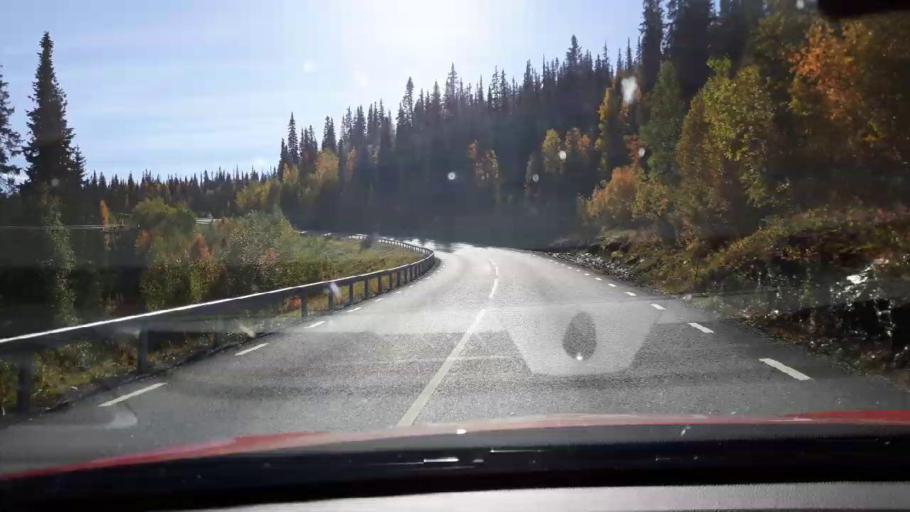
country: NO
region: Nord-Trondelag
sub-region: Royrvik
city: Royrvik
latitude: 64.8523
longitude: 14.1780
